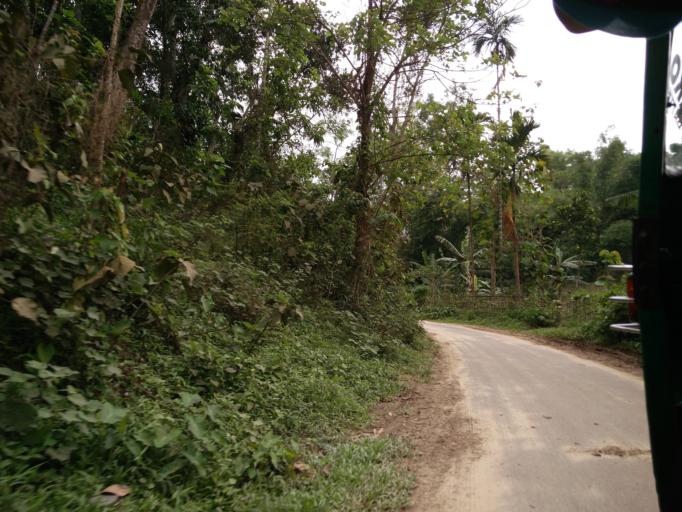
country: IN
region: Tripura
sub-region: Dhalai
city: Kamalpur
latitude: 24.3027
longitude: 91.7879
